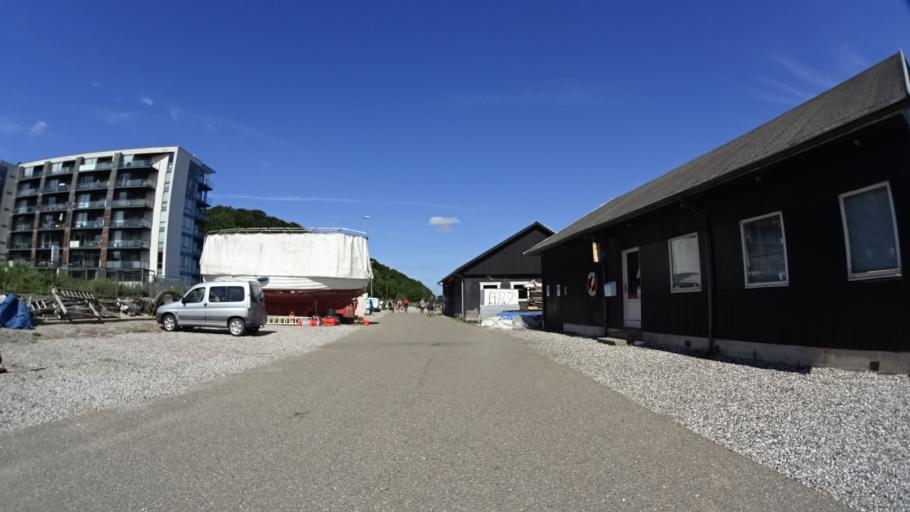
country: DK
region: Central Jutland
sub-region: Arhus Kommune
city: Arhus
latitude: 56.1685
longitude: 10.2217
